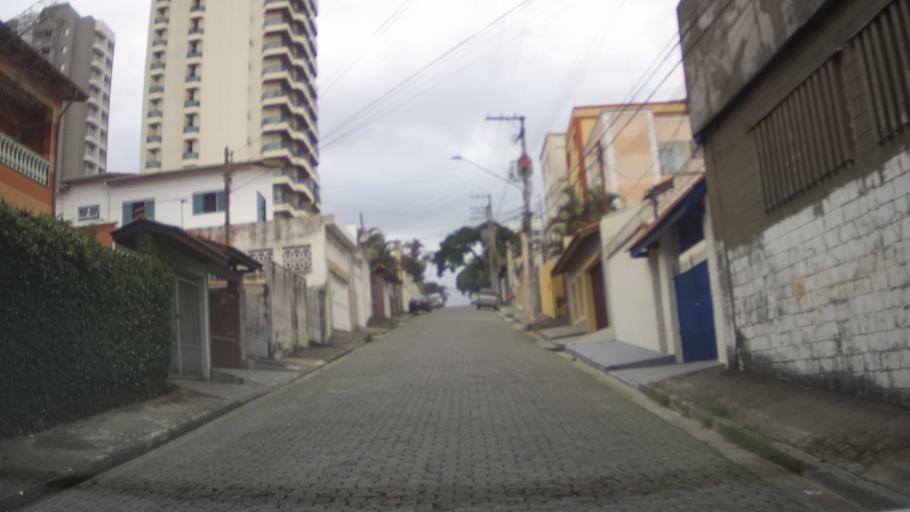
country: BR
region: Sao Paulo
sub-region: Guarulhos
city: Guarulhos
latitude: -23.4579
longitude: -46.5623
